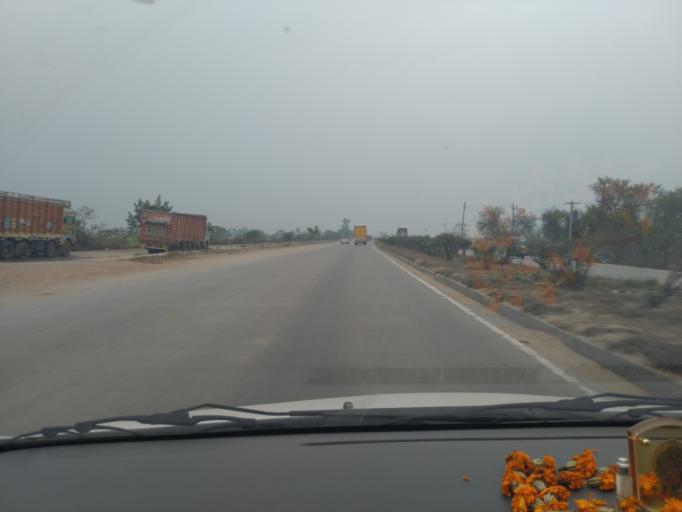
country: IN
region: Bihar
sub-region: Rohtas
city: Dehri
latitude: 24.9670
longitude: 83.9261
